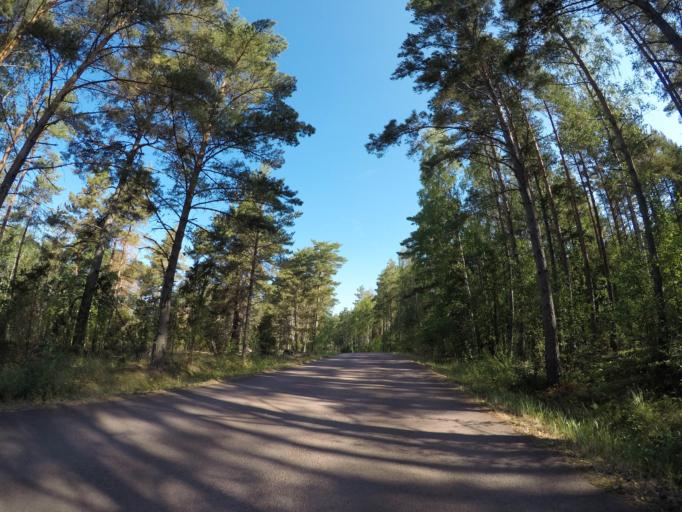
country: AX
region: Alands landsbygd
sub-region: Finstroem
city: Finstroem
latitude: 60.3313
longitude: 19.9113
